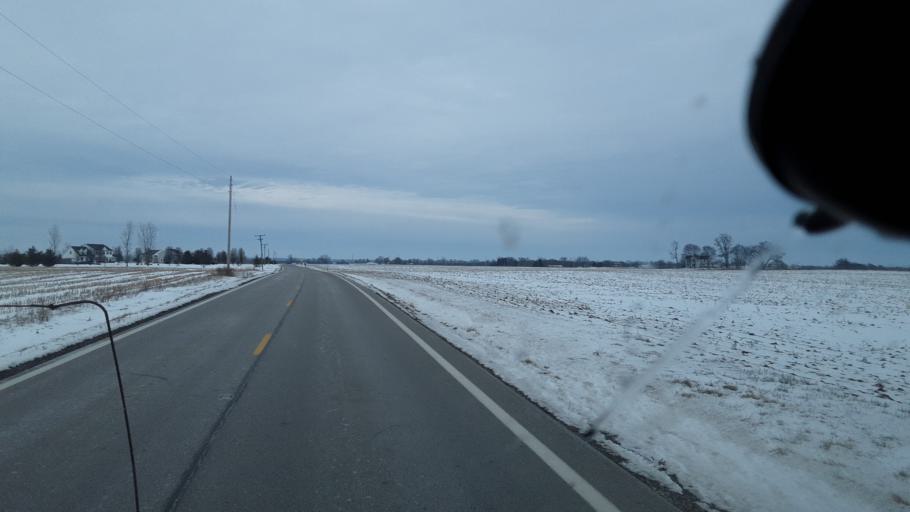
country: US
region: Ohio
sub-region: Pickaway County
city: Williamsport
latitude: 39.6318
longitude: -83.0637
